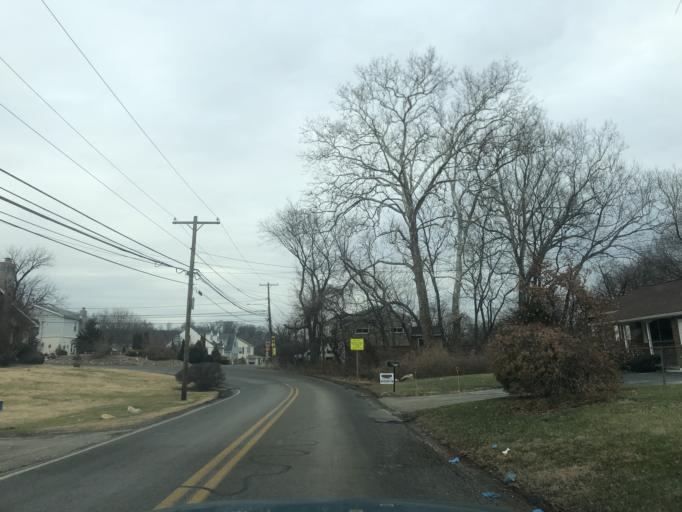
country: US
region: Pennsylvania
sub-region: Montgomery County
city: Bridgeport
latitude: 40.0946
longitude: -75.3492
